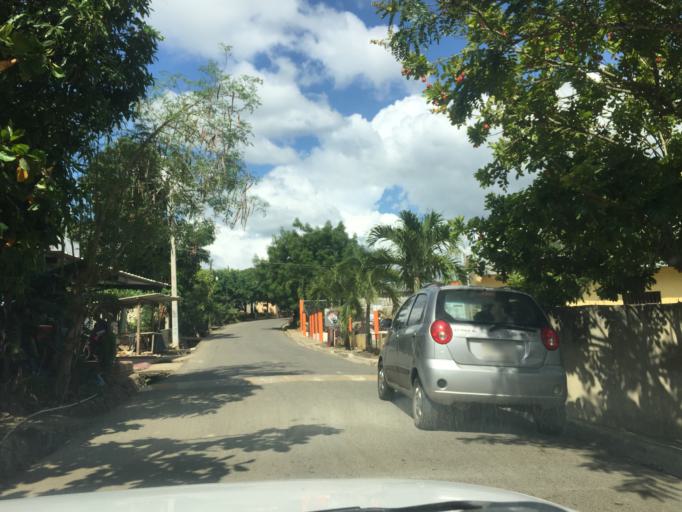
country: DO
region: La Vega
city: Rio Verde Arriba
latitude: 19.3587
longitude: -70.5944
